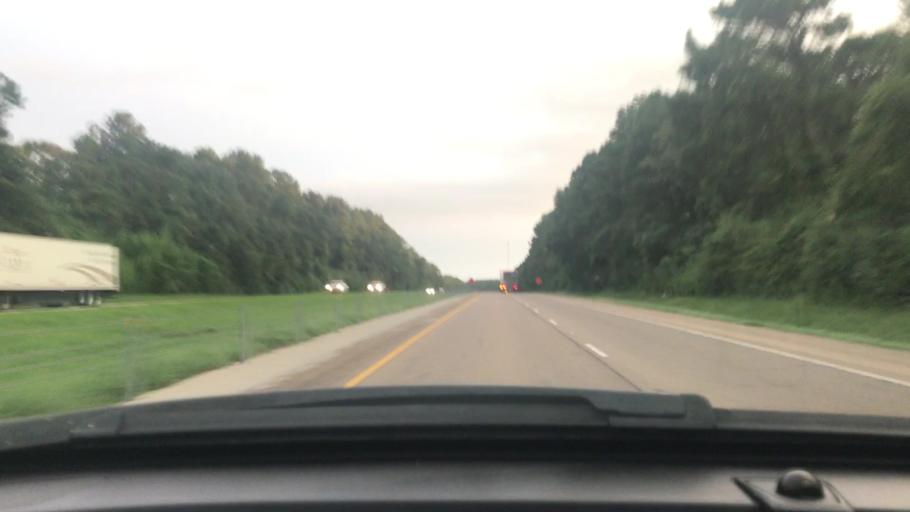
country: US
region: Louisiana
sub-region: Tangipahoa Parish
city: Kentwood
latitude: 30.9632
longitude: -90.5174
